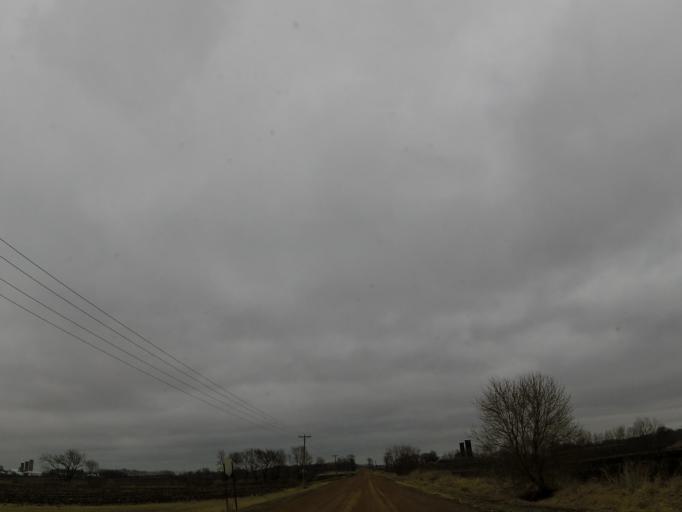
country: US
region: Minnesota
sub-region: Scott County
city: Jordan
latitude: 44.7033
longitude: -93.5388
